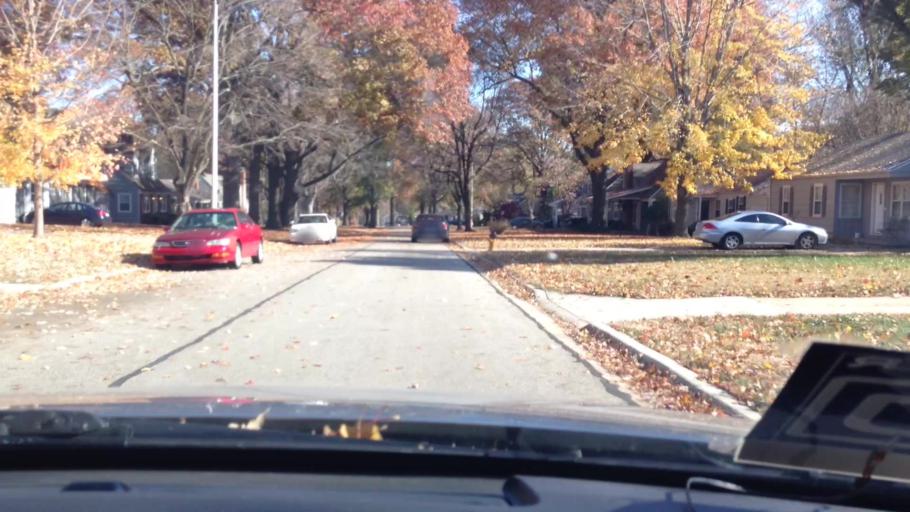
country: US
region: Kansas
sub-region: Johnson County
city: Prairie Village
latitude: 39.0013
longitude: -94.6478
